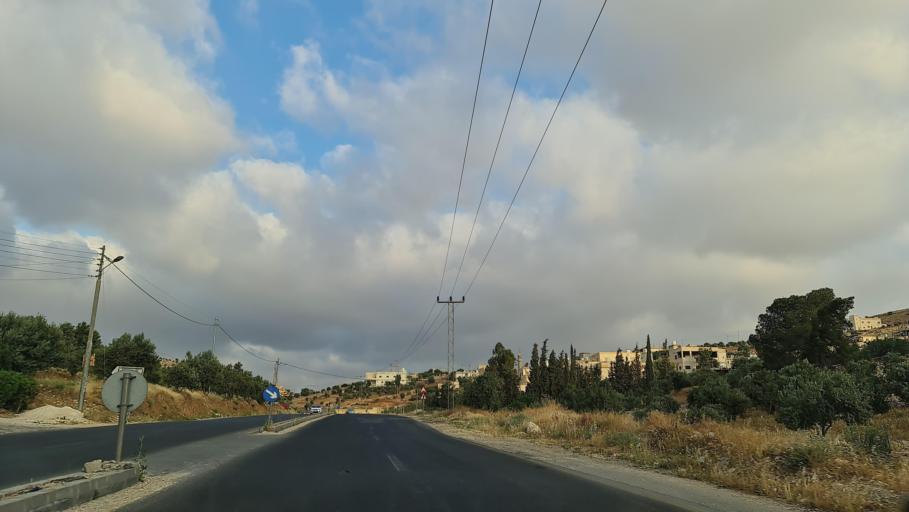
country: JO
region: Amman
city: Al Jubayhah
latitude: 32.0920
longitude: 35.9483
